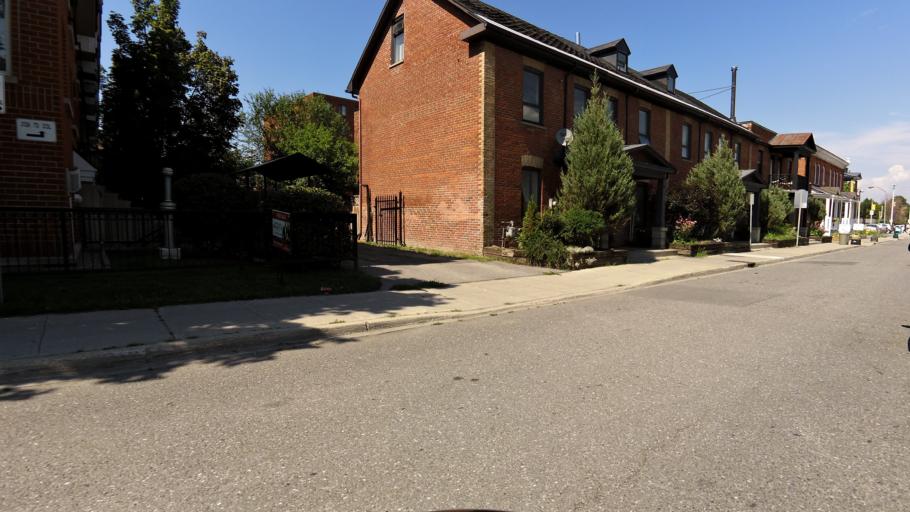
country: CA
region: Ontario
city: Ottawa
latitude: 45.4319
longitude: -75.6903
